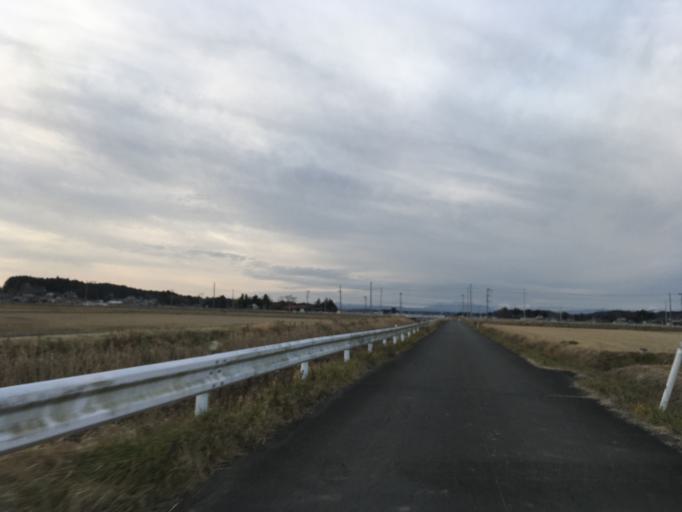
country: JP
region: Miyagi
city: Kogota
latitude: 38.6452
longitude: 141.0586
